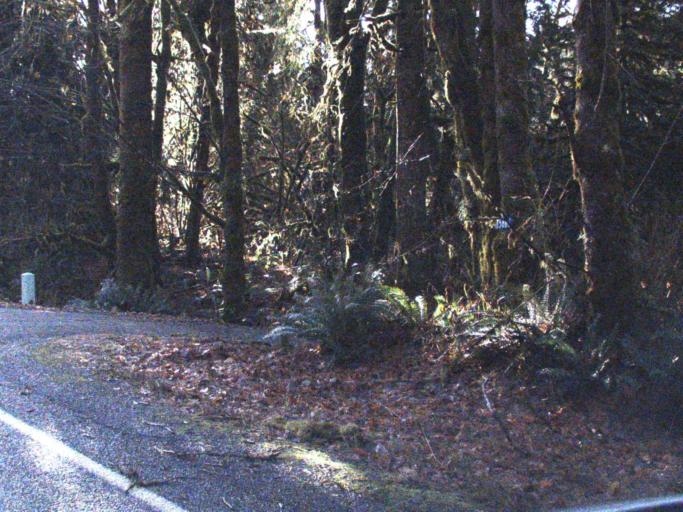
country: US
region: Washington
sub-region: Snohomish County
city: Darrington
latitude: 48.4152
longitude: -121.5579
